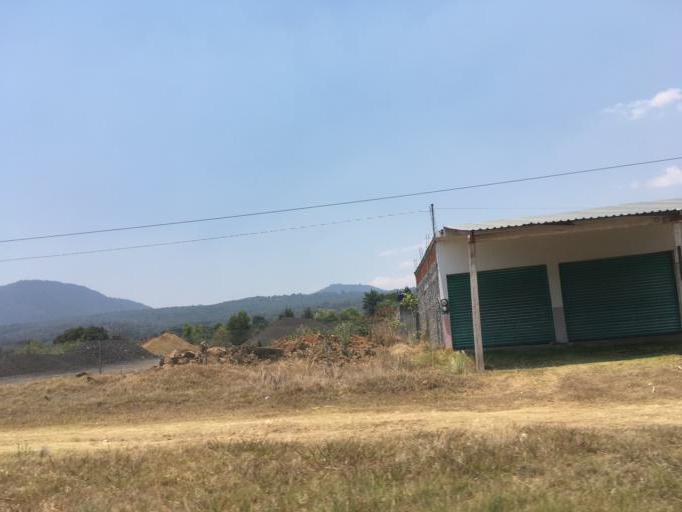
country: MX
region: Michoacan
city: Quiroga
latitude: 19.6464
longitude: -101.4916
